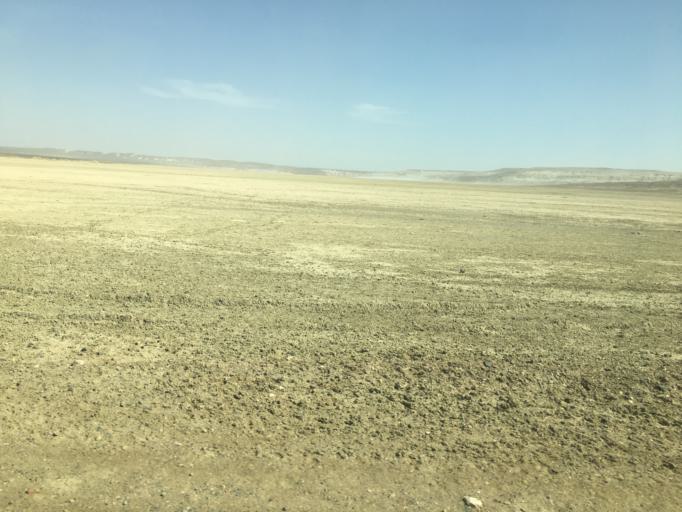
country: TM
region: Balkan
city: Balkanabat
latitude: 40.3685
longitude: 54.3933
